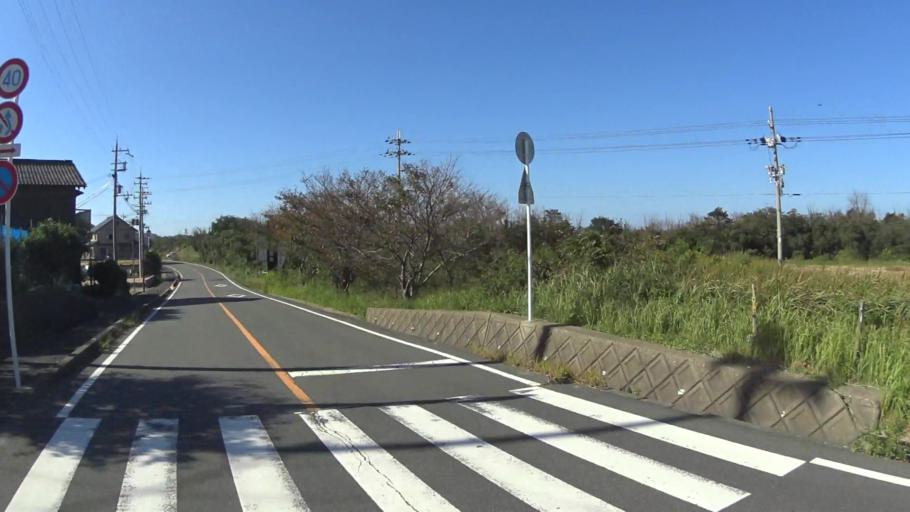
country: JP
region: Hyogo
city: Toyooka
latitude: 35.6429
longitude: 134.9138
